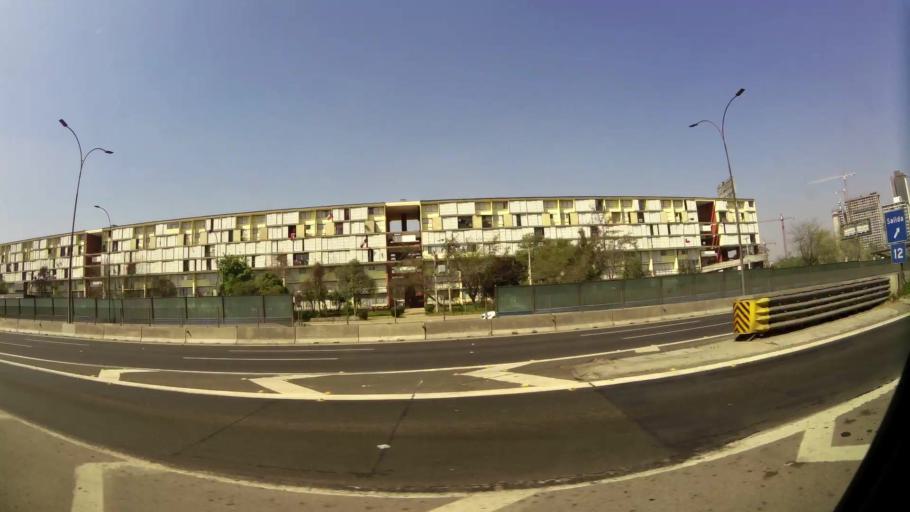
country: CL
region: Santiago Metropolitan
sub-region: Provincia de Santiago
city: Lo Prado
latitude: -33.4484
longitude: -70.6930
